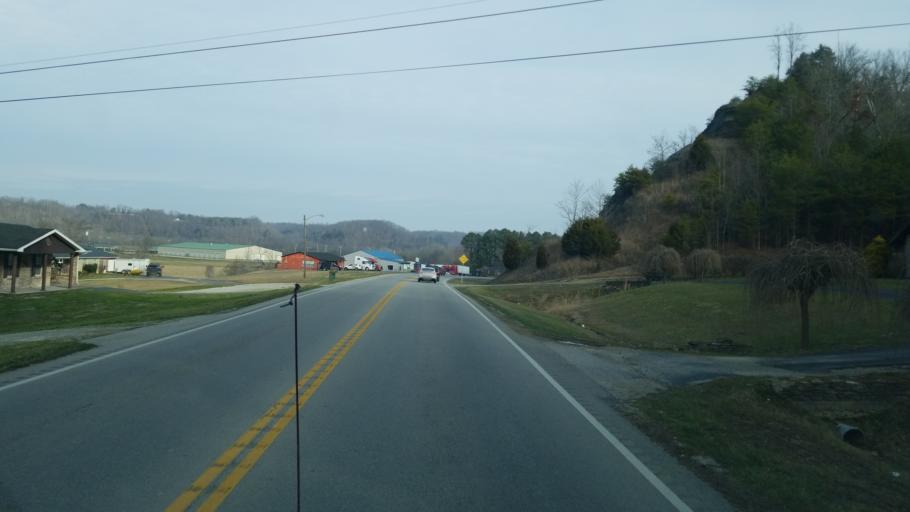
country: US
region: Kentucky
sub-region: Casey County
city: Liberty
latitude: 37.3052
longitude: -84.9456
